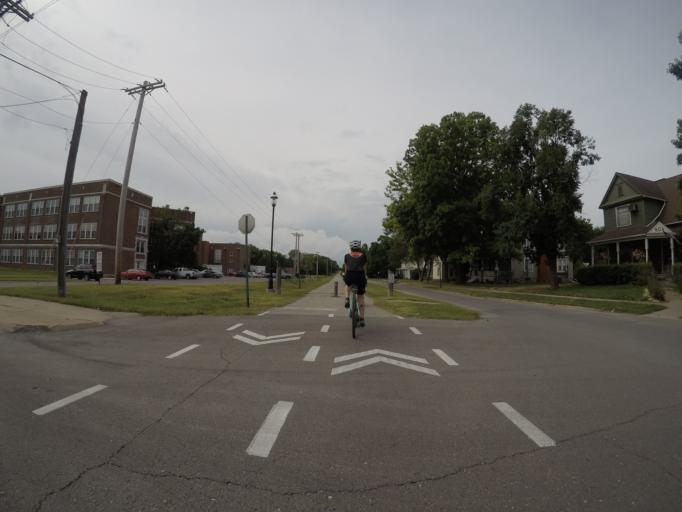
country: US
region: Kansas
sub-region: Franklin County
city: Ottawa
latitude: 38.6113
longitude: -95.2700
